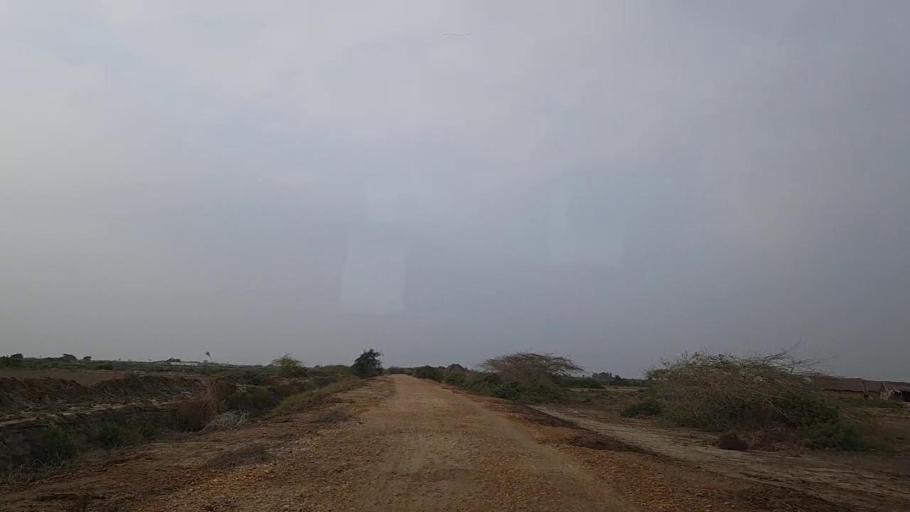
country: PK
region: Sindh
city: Mirpur Sakro
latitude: 24.6116
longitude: 67.5154
